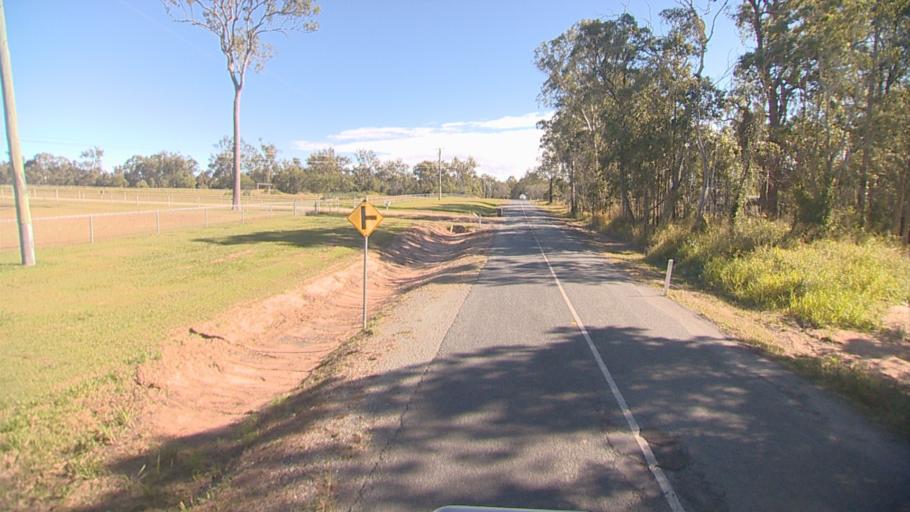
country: AU
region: Queensland
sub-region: Logan
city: Chambers Flat
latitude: -27.7921
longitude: 153.0763
